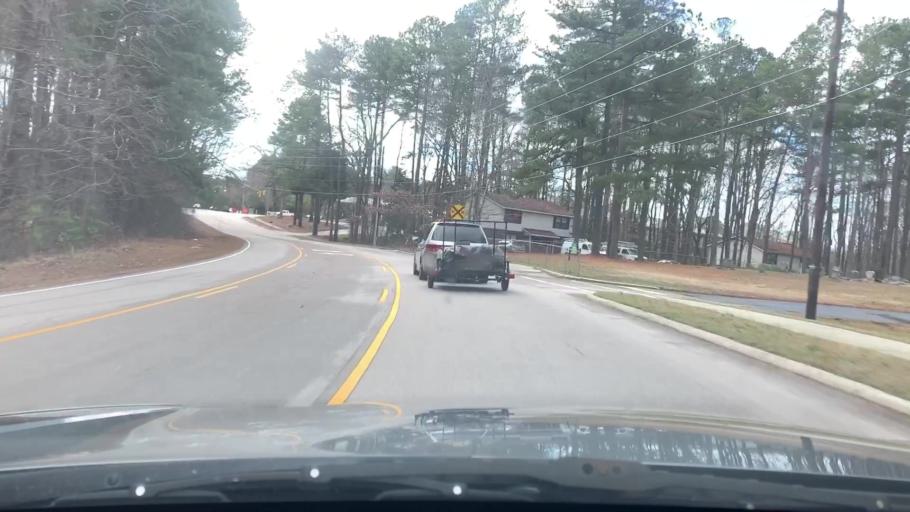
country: US
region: North Carolina
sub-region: Wake County
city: Cary
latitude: 35.7851
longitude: -78.7988
